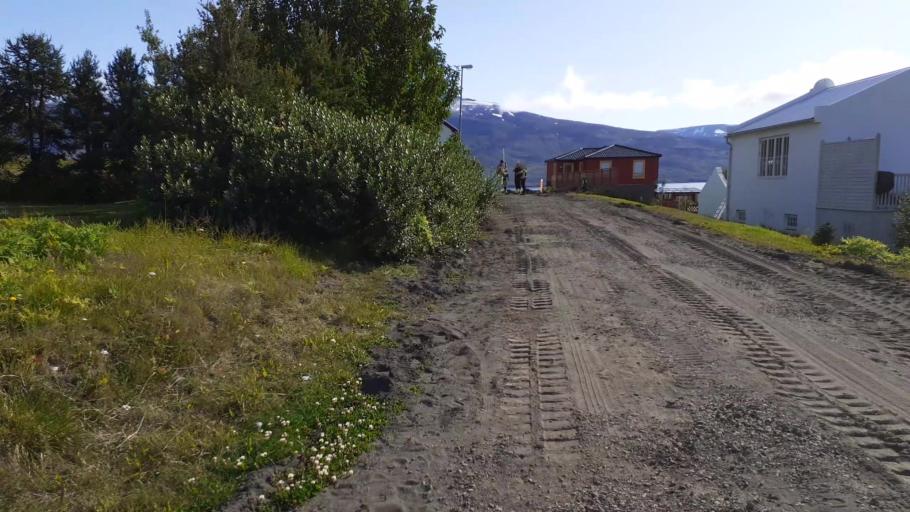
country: IS
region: Northeast
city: Dalvik
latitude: 65.9779
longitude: -18.3671
